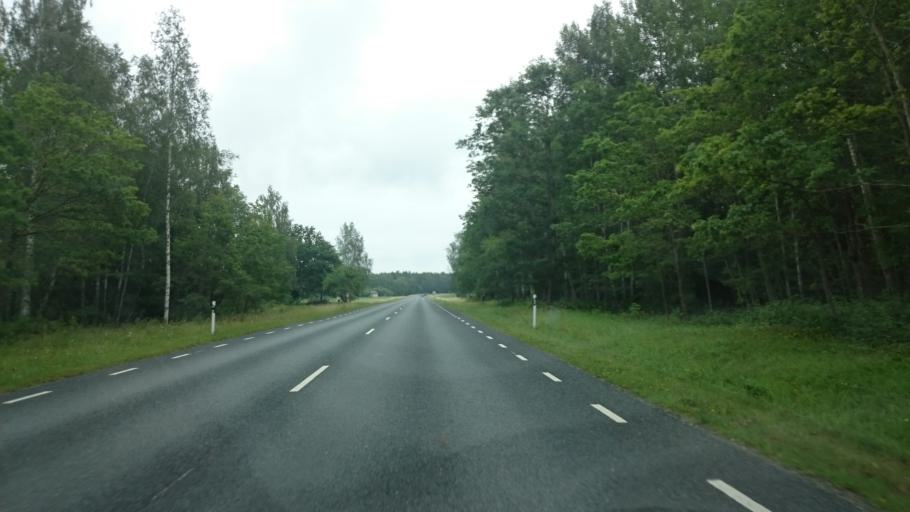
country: EE
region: Saare
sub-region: Orissaare vald
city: Orissaare
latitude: 58.6026
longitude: 23.3093
